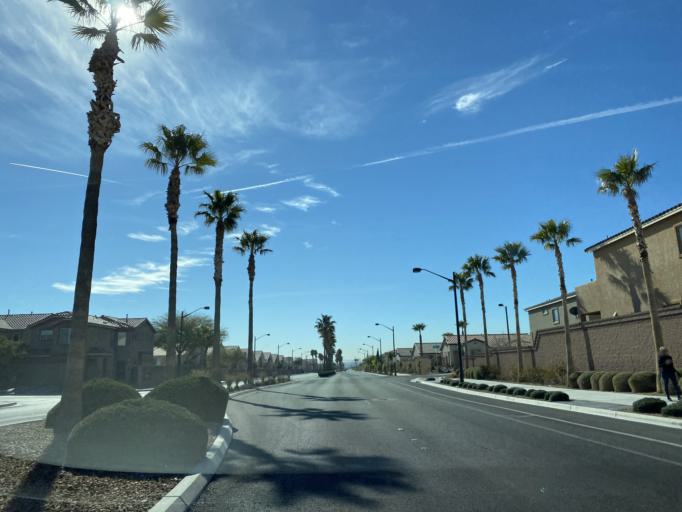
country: US
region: Nevada
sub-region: Clark County
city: Summerlin South
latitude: 36.2907
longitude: -115.2970
